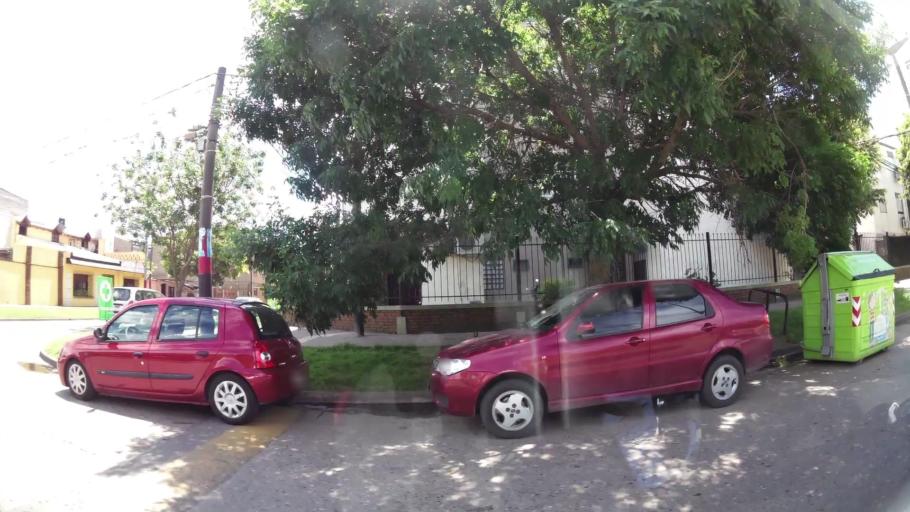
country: AR
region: Santa Fe
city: Gobernador Galvez
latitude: -32.9933
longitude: -60.6228
